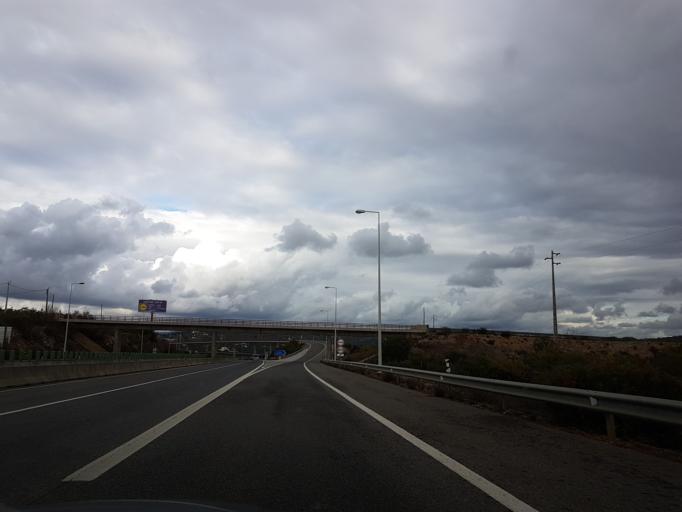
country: PT
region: Faro
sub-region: Albufeira
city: Ferreiras
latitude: 37.1511
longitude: -8.2134
